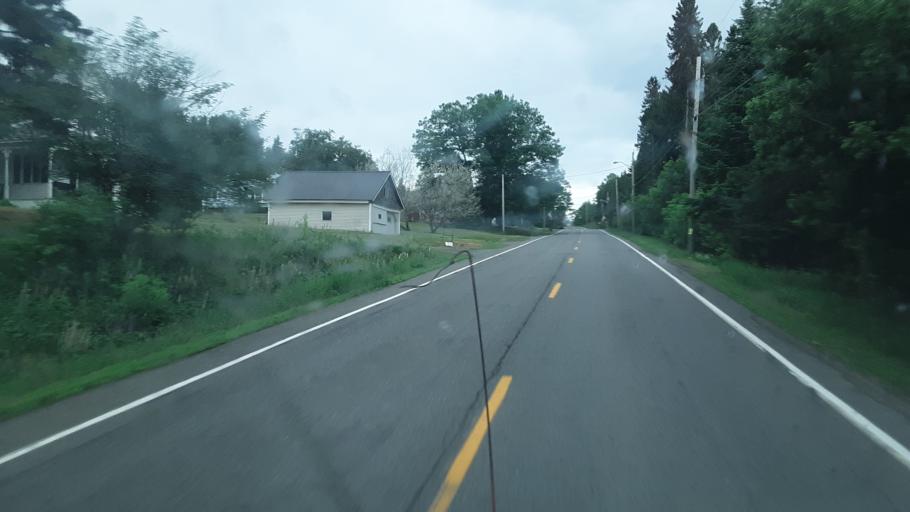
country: US
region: Maine
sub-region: Aroostook County
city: Presque Isle
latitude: 46.4976
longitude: -68.3692
